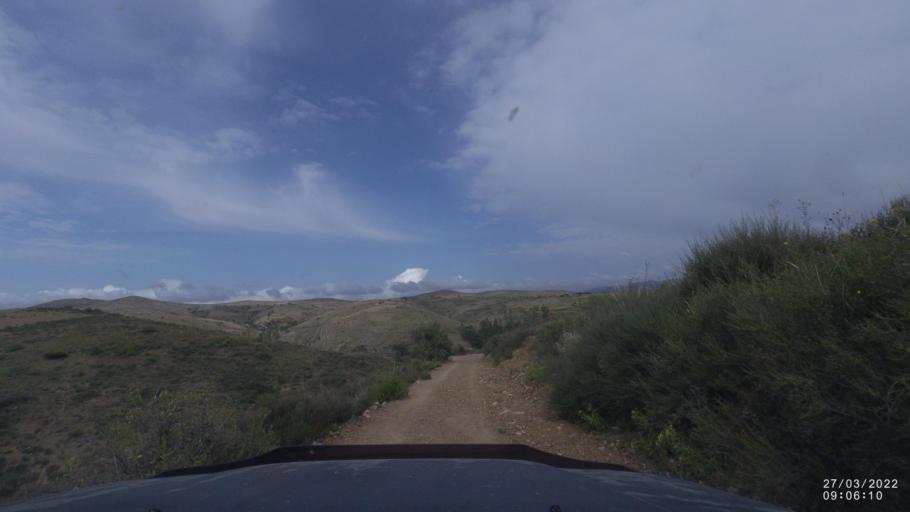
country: BO
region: Cochabamba
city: Cliza
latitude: -17.7317
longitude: -65.8707
